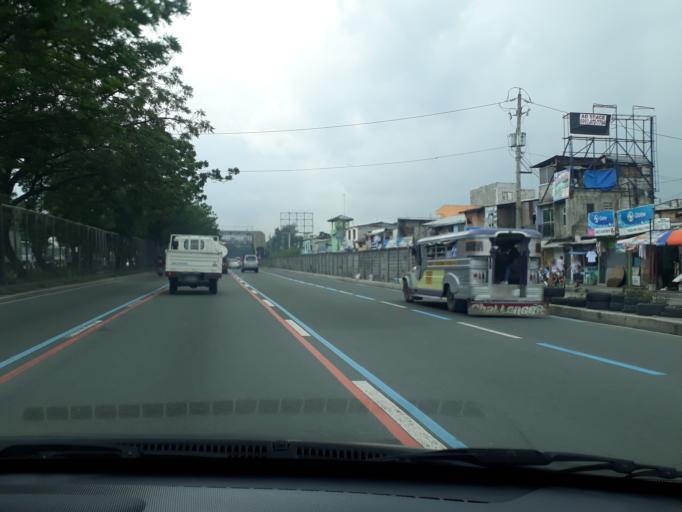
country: PH
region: Calabarzon
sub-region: Province of Rizal
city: Pateros
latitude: 14.5248
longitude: 121.0552
